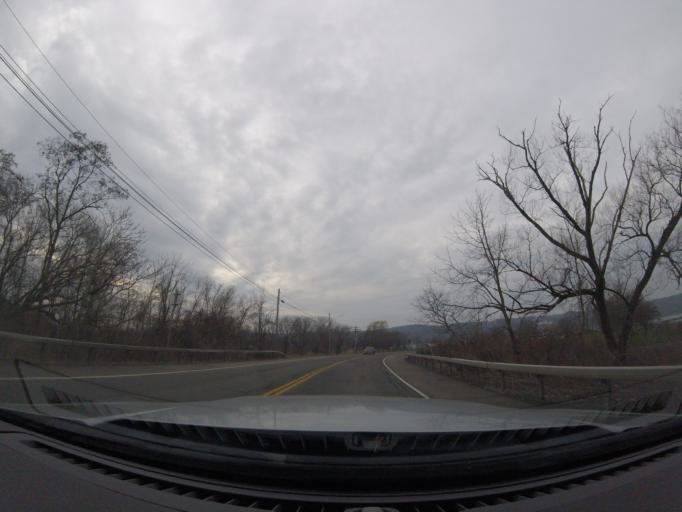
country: US
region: New York
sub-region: Schuyler County
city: Watkins Glen
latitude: 42.3864
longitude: -76.8555
